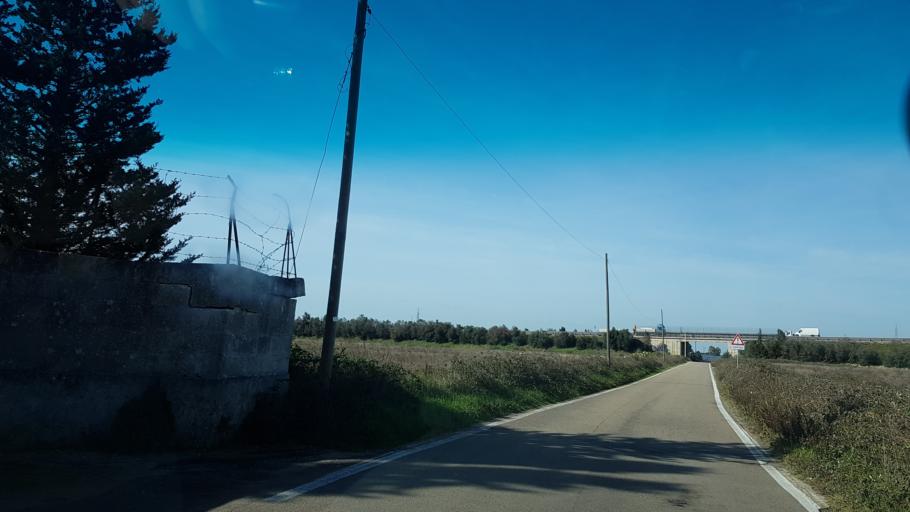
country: IT
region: Apulia
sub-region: Provincia di Lecce
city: Arnesano
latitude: 40.3499
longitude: 18.1297
